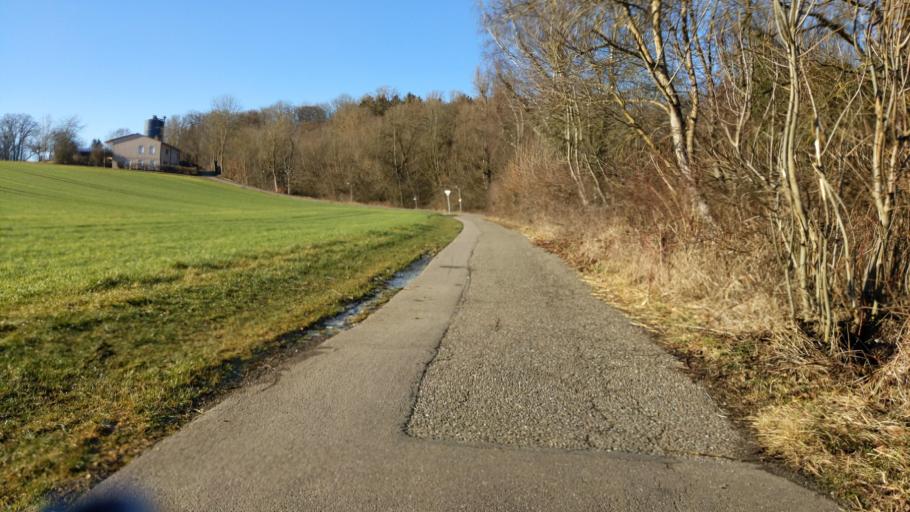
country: DE
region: Baden-Wuerttemberg
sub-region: Regierungsbezirk Stuttgart
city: Rutesheim
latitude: 48.7881
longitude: 8.9585
